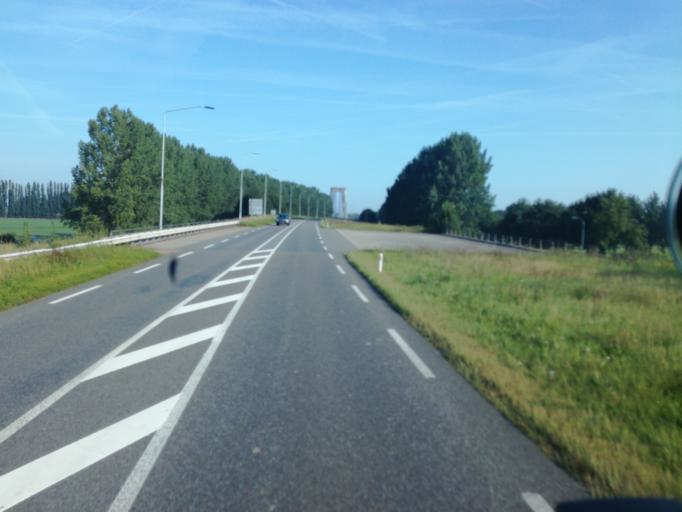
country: NL
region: North Brabant
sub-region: Gemeente Heusden
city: Heusden
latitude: 51.7299
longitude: 5.1207
